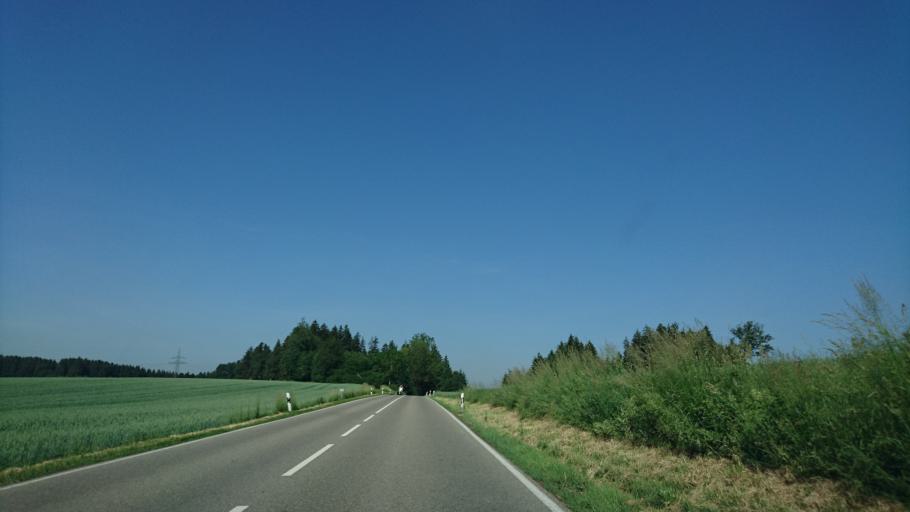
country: DE
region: Bavaria
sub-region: Swabia
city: Horgau
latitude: 48.3629
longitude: 10.6704
